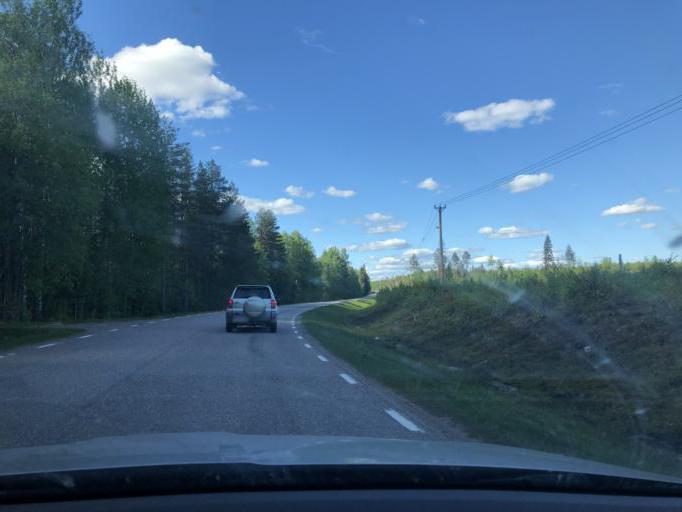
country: SE
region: Norrbotten
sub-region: Kalix Kommun
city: Kalix
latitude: 65.9303
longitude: 23.1602
